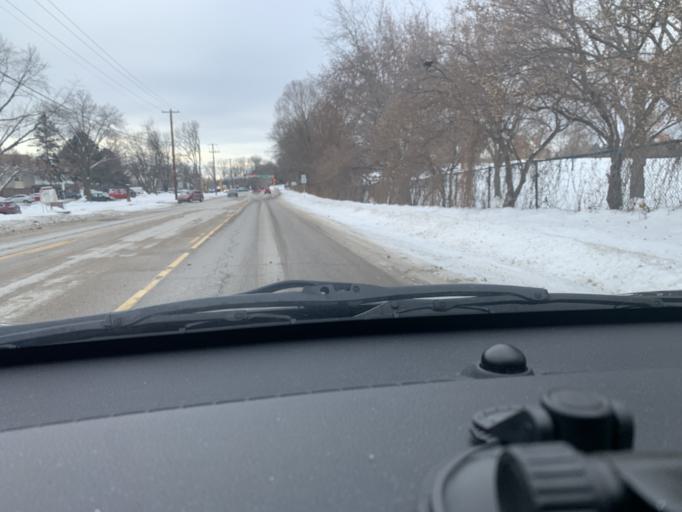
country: US
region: Minnesota
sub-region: Dakota County
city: South Saint Paul
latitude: 44.8856
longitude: -93.0704
